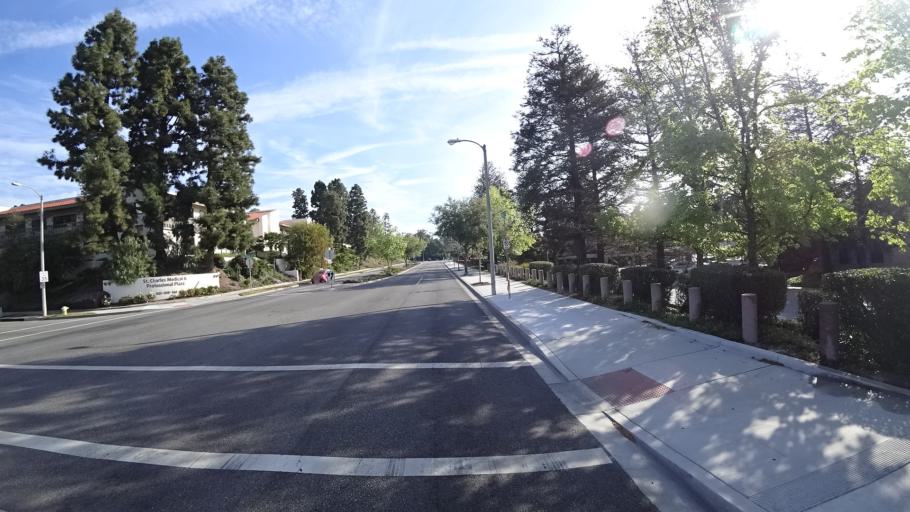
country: US
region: California
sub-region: Ventura County
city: Thousand Oaks
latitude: 34.1851
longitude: -118.8776
